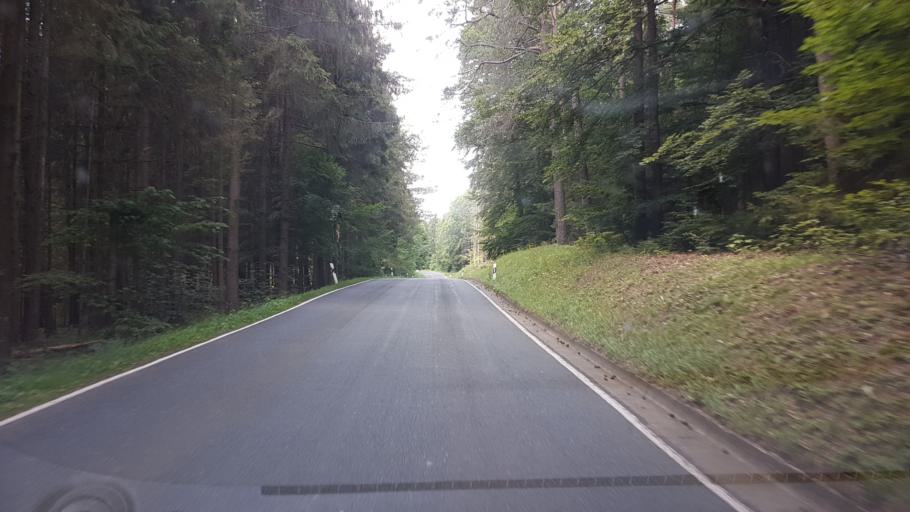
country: DE
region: Bavaria
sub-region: Upper Franconia
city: Gossweinstein
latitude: 49.7637
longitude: 11.2797
